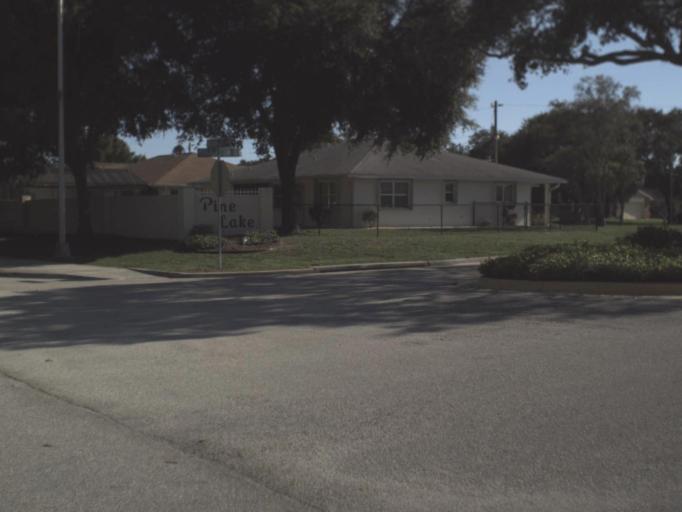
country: US
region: Florida
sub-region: Sarasota County
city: Englewood
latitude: 26.9878
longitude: -82.3659
